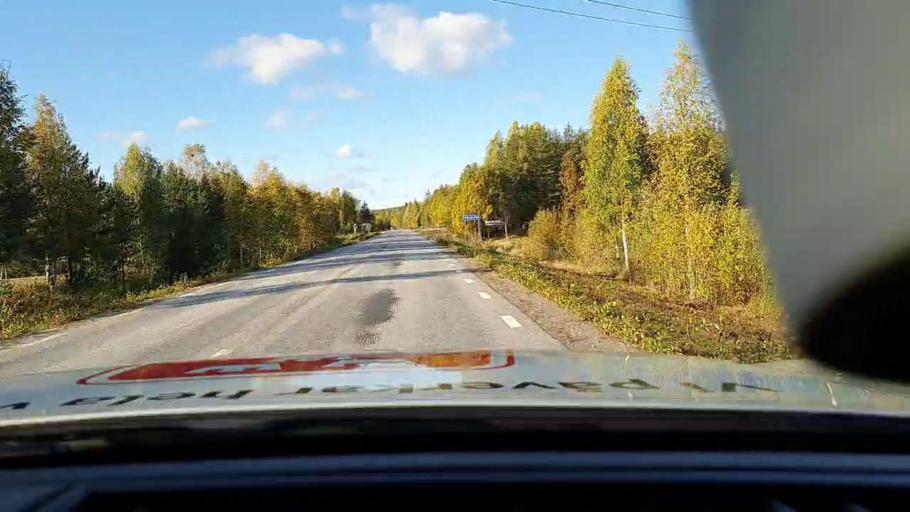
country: SE
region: Norrbotten
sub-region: Pitea Kommun
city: Norrfjarden
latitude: 65.4590
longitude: 21.4540
